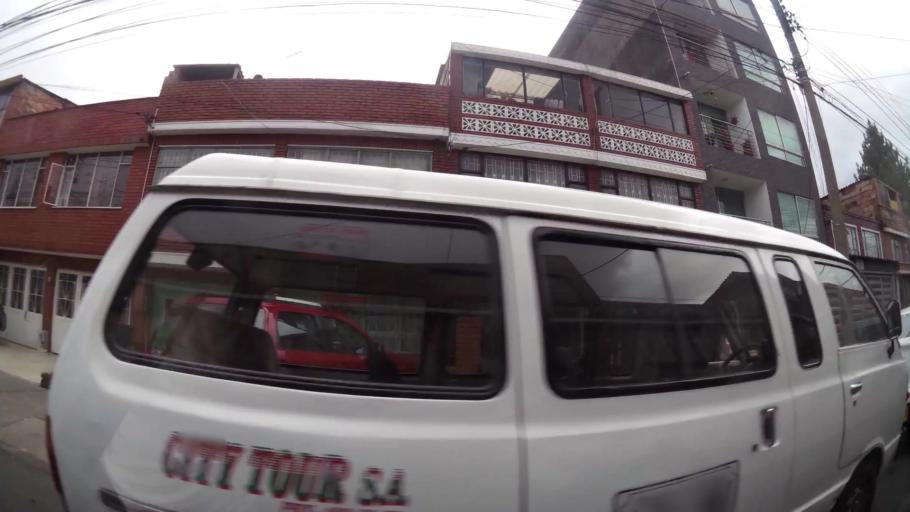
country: CO
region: Bogota D.C.
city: Bogota
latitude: 4.6872
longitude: -74.1055
